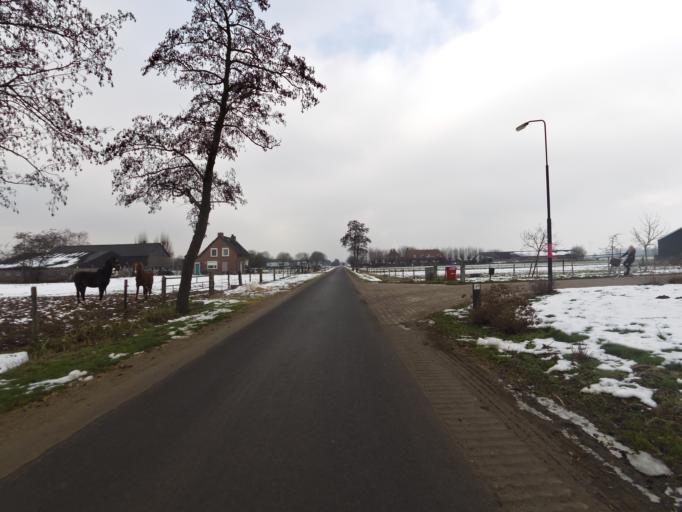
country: NL
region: Gelderland
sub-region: Gemeente Duiven
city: Duiven
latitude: 51.9525
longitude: 6.0396
